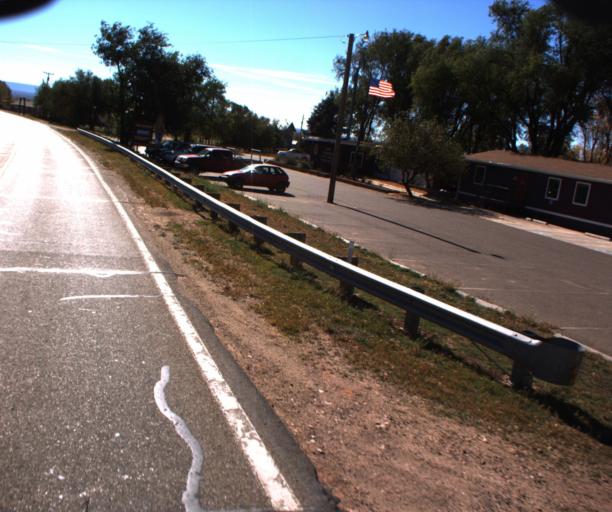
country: US
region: Arizona
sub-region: Coconino County
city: Fredonia
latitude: 36.9422
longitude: -112.5255
